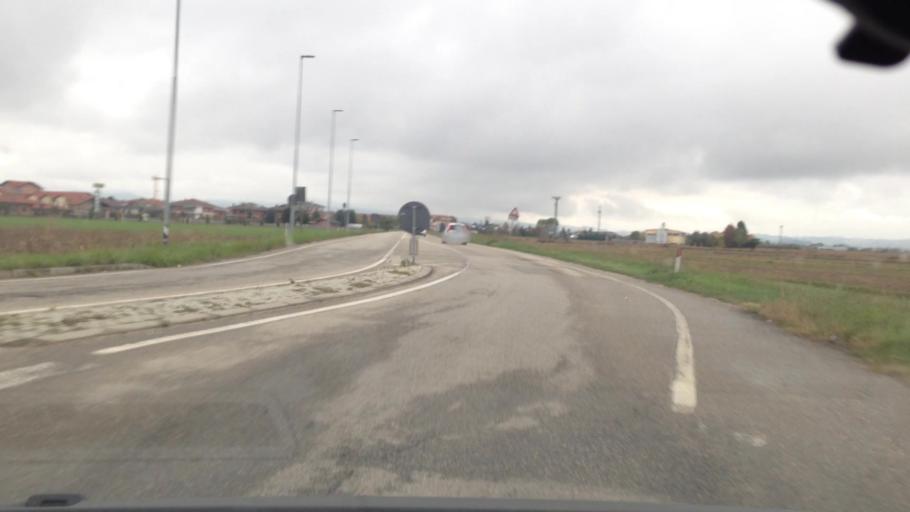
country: IT
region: Piedmont
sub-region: Provincia di Torino
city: Riva Presso Chieri
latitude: 44.9760
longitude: 7.8827
